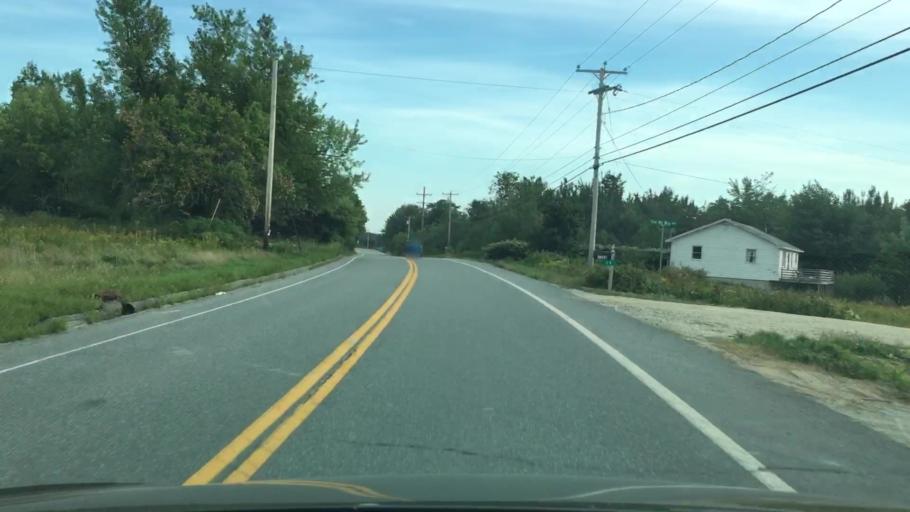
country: US
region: Maine
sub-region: Hancock County
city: Penobscot
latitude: 44.4707
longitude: -68.7817
